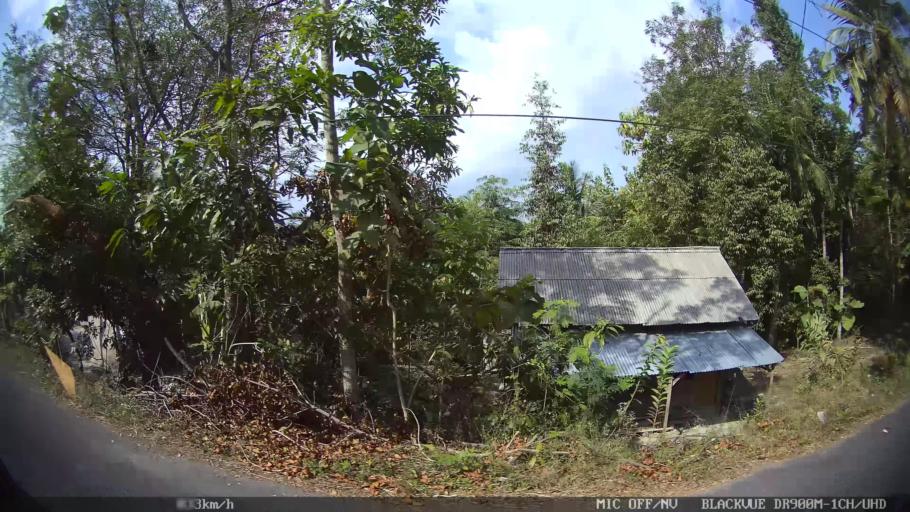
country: ID
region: Daerah Istimewa Yogyakarta
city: Kasihan
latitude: -7.8486
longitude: 110.3004
